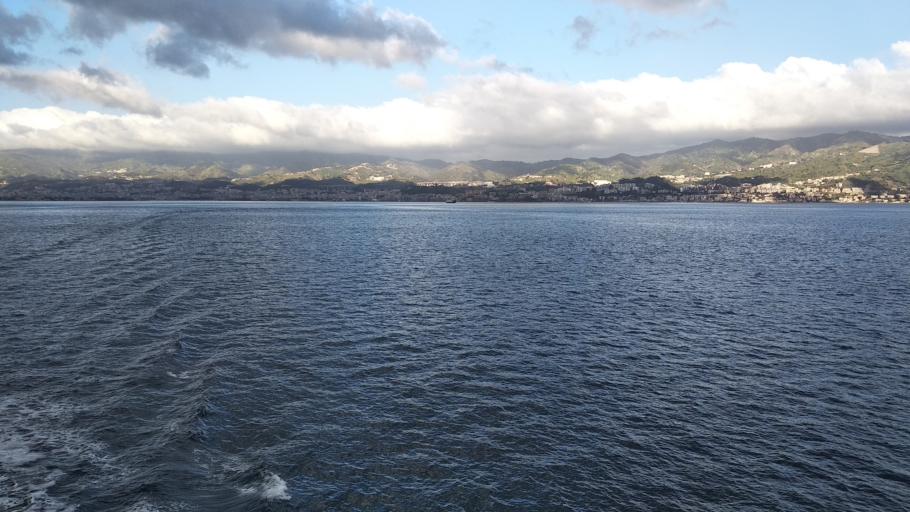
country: IT
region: Calabria
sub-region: Provincia di Reggio Calabria
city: Campo Calabro
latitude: 38.2122
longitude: 15.6130
